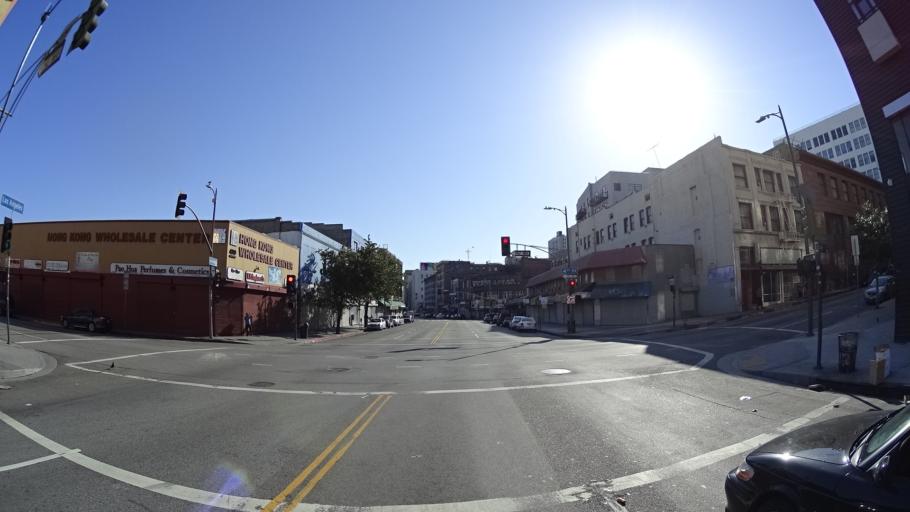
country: US
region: California
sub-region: Los Angeles County
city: Los Angeles
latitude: 34.0475
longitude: -118.2460
